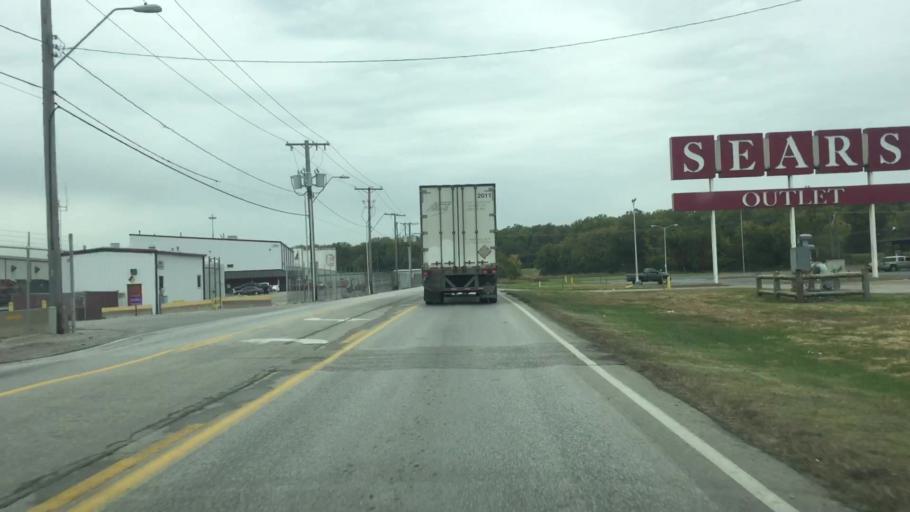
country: US
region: Missouri
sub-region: Clay County
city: North Kansas City
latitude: 39.1313
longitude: -94.5371
